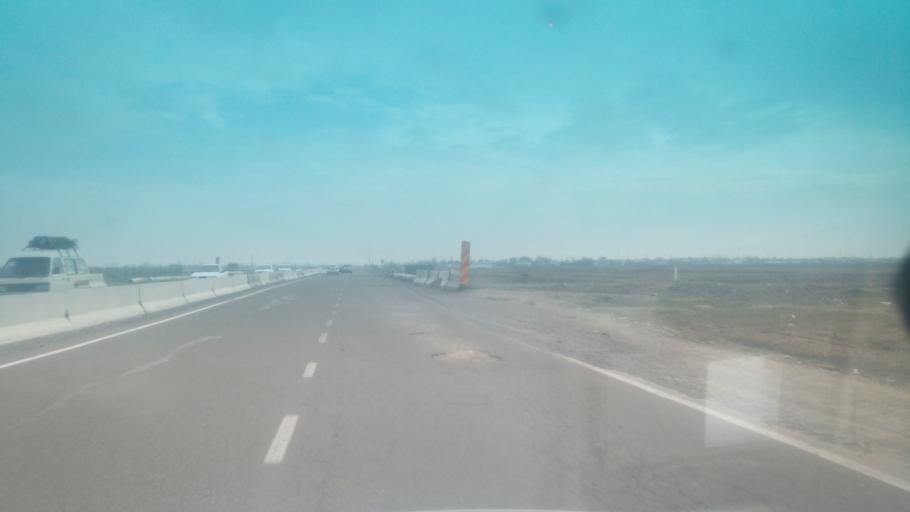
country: KZ
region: Ongtustik Qazaqstan
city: Myrzakent
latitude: 40.5108
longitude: 68.4979
